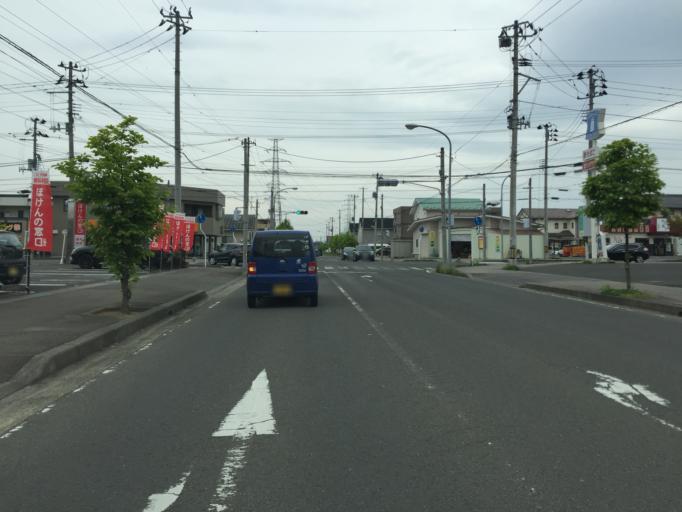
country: JP
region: Fukushima
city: Fukushima-shi
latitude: 37.7902
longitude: 140.4447
